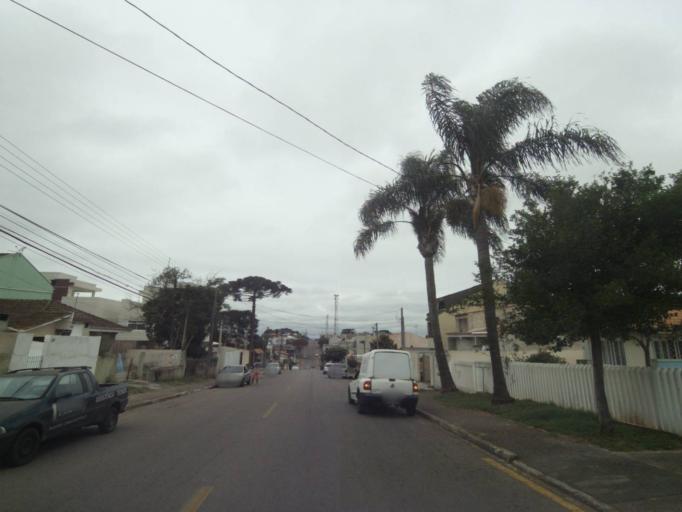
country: BR
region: Parana
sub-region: Sao Jose Dos Pinhais
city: Sao Jose dos Pinhais
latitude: -25.4831
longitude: -49.2310
